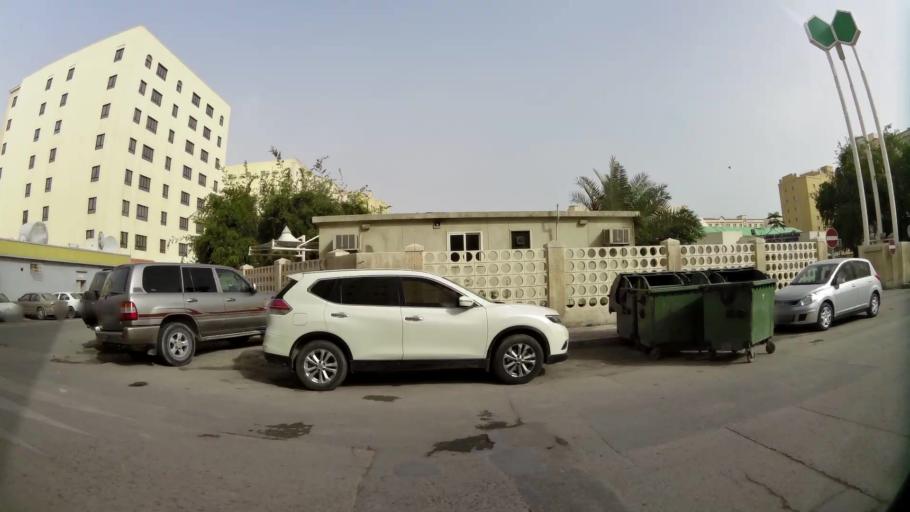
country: QA
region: Baladiyat ad Dawhah
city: Doha
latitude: 25.2766
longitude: 51.5455
